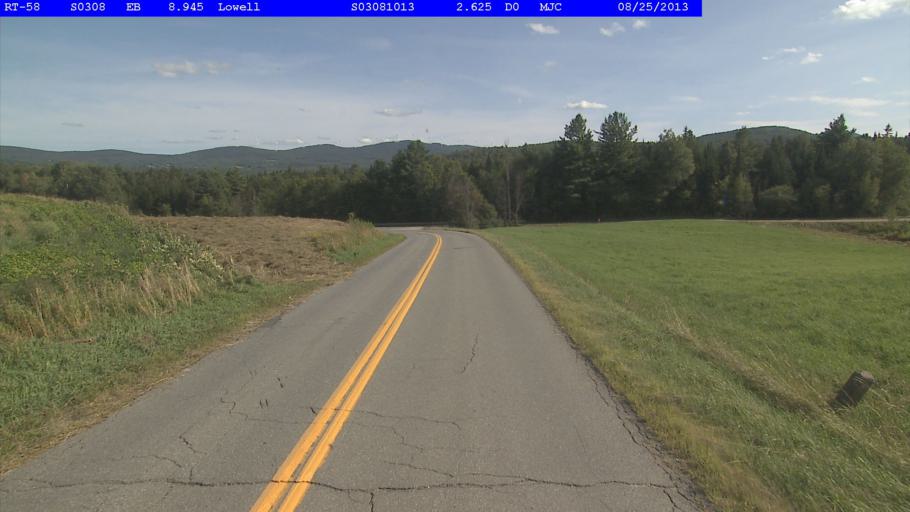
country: US
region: Vermont
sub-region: Lamoille County
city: Hyde Park
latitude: 44.8132
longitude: -72.4671
